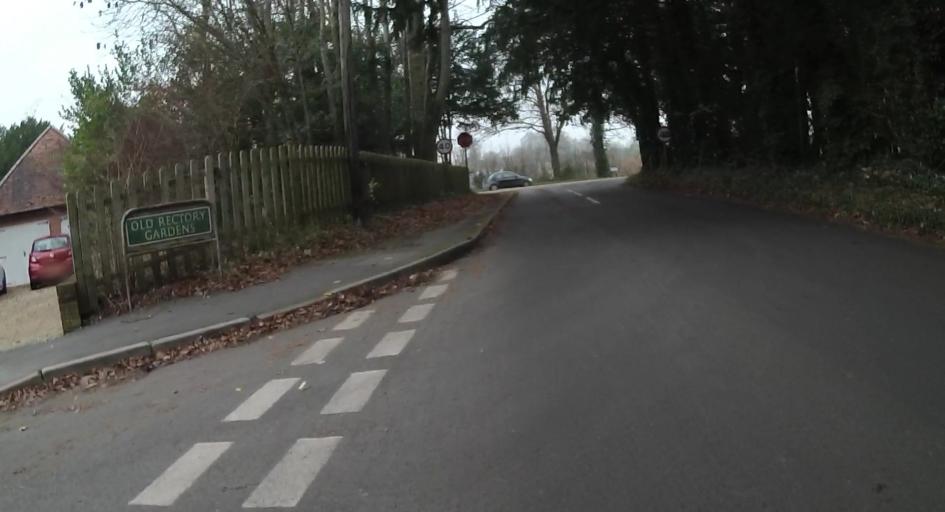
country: GB
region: England
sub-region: Hampshire
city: Kings Worthy
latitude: 51.0930
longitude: -1.2917
